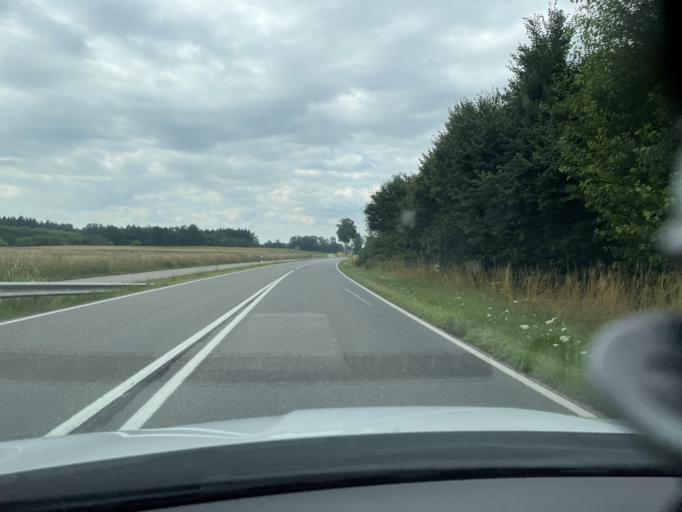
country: DE
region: Bavaria
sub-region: Upper Bavaria
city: Sankt Wolfgang
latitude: 48.1871
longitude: 12.1483
